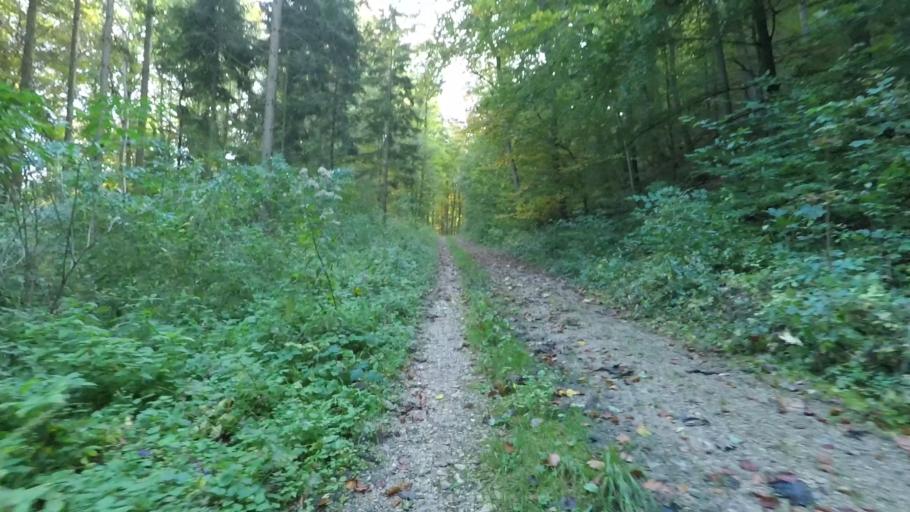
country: DE
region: Baden-Wuerttemberg
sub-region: Tuebingen Region
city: Pfullingen
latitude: 48.4445
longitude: 9.2326
